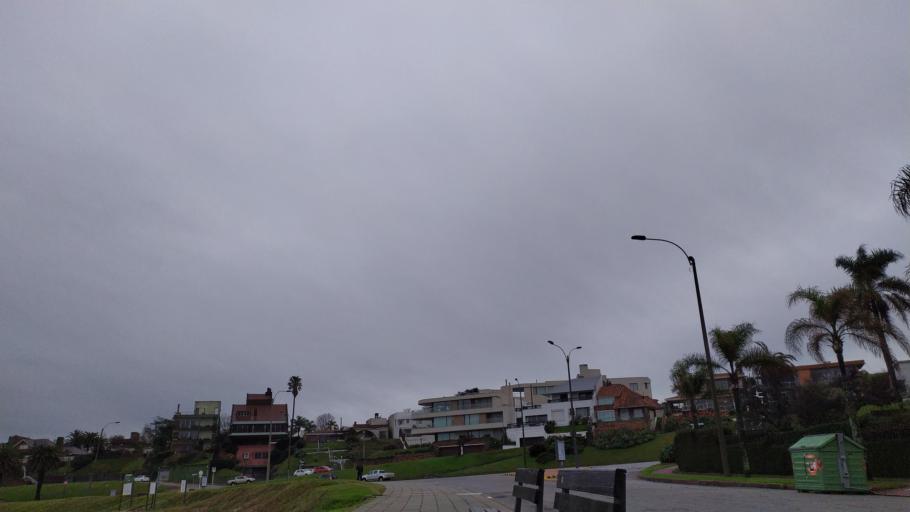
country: UY
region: Canelones
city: Paso de Carrasco
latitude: -34.8959
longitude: -56.0840
